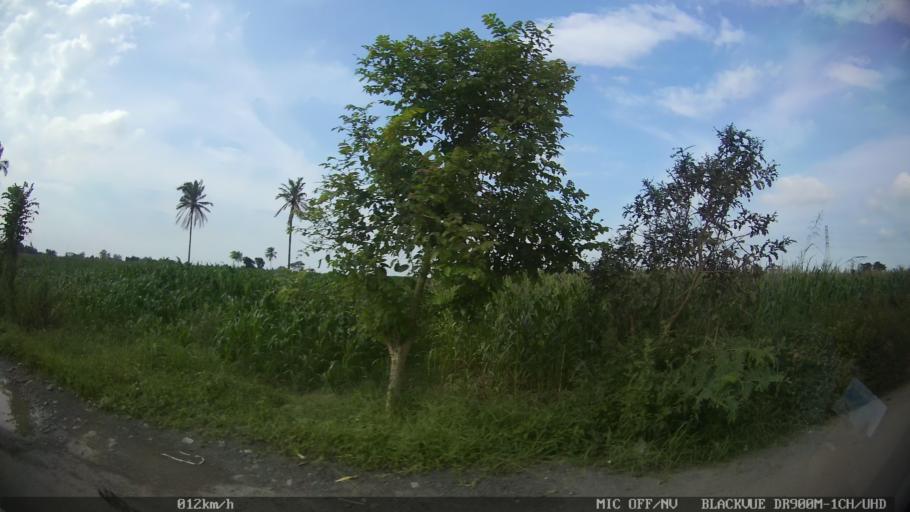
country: ID
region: North Sumatra
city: Percut
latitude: 3.5692
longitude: 98.7798
